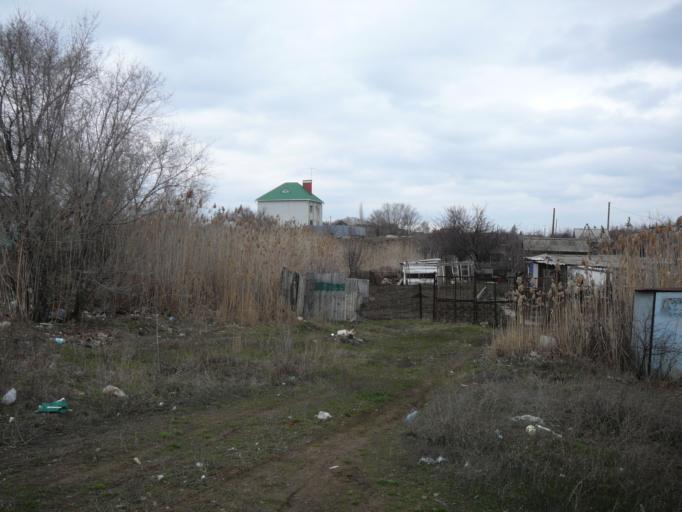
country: RU
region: Saratov
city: Engel's
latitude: 51.4650
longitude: 46.0979
